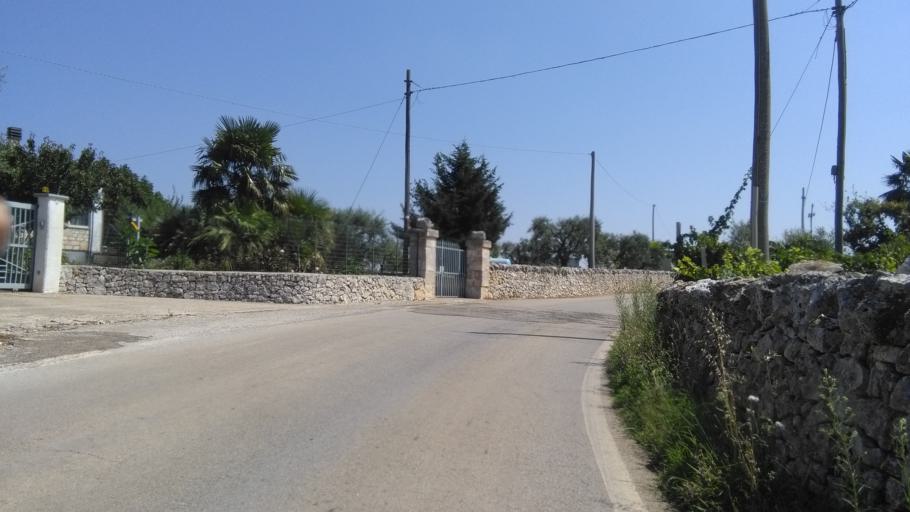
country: IT
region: Apulia
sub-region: Provincia di Bari
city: Alberobello
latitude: 40.7988
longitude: 17.2151
